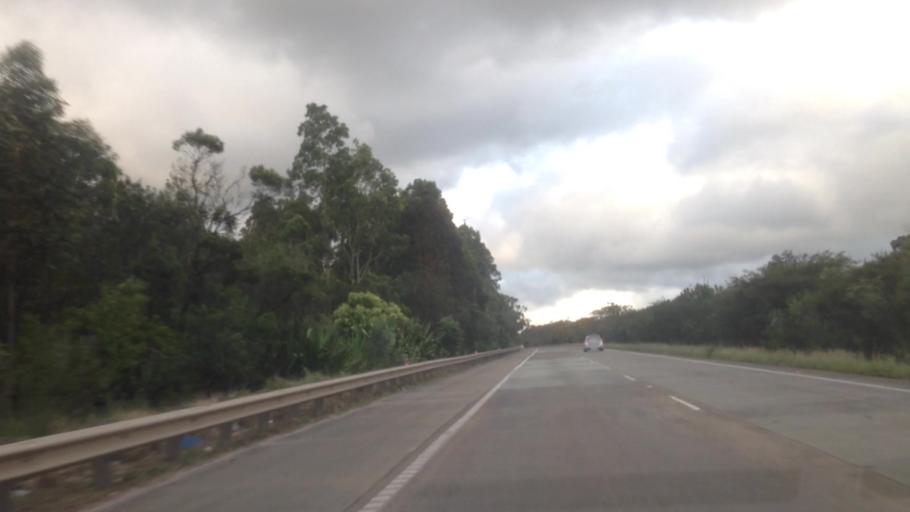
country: AU
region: New South Wales
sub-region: Wyong Shire
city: Jilliby
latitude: -33.2037
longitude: 151.4590
